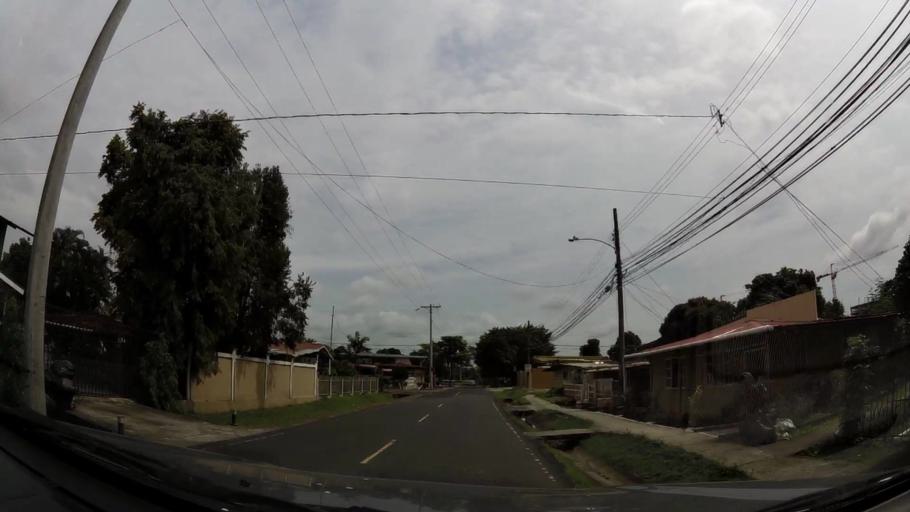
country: PA
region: Panama
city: San Miguelito
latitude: 9.0414
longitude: -79.4238
